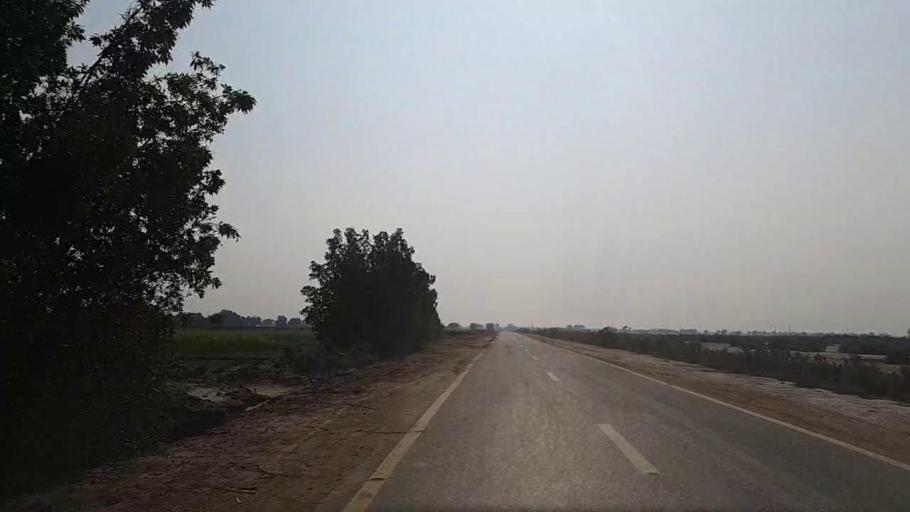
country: PK
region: Sindh
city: Jam Sahib
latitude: 26.3699
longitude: 68.5367
